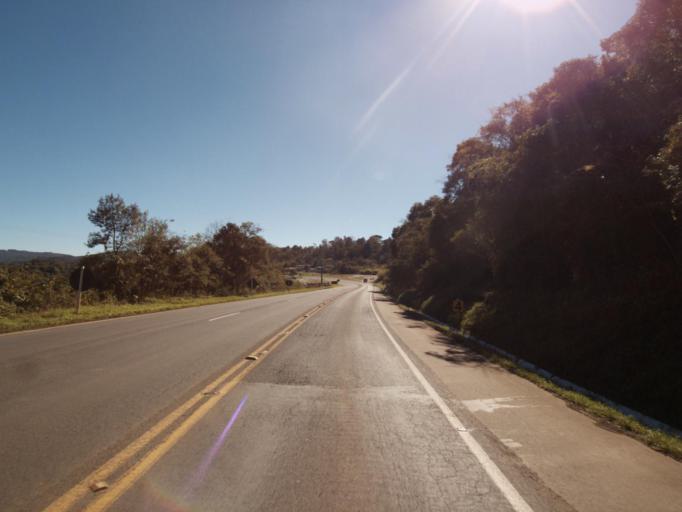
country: BR
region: Santa Catarina
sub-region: Joacaba
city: Joacaba
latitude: -27.1698
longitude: -51.5597
